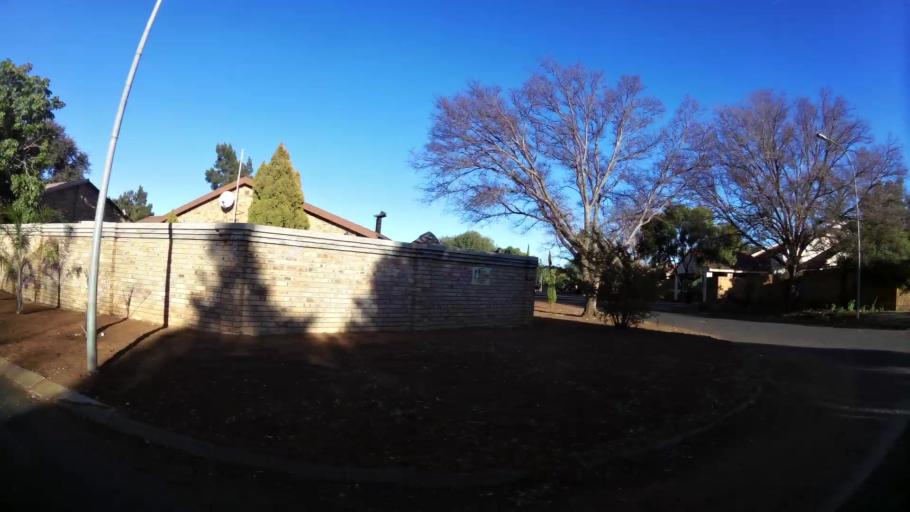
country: ZA
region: Northern Cape
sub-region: Frances Baard District Municipality
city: Kimberley
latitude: -28.7577
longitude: 24.7558
